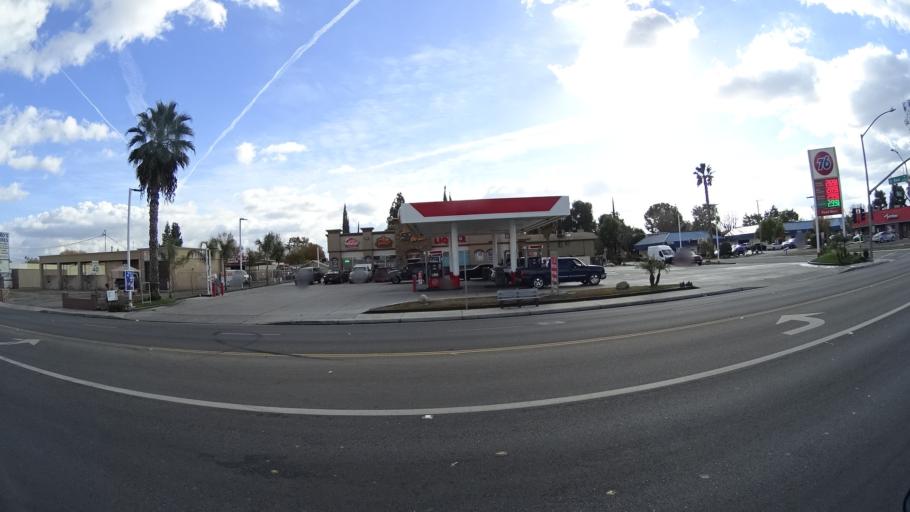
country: US
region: California
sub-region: Kern County
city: Bakersfield
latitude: 35.3324
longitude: -119.0430
